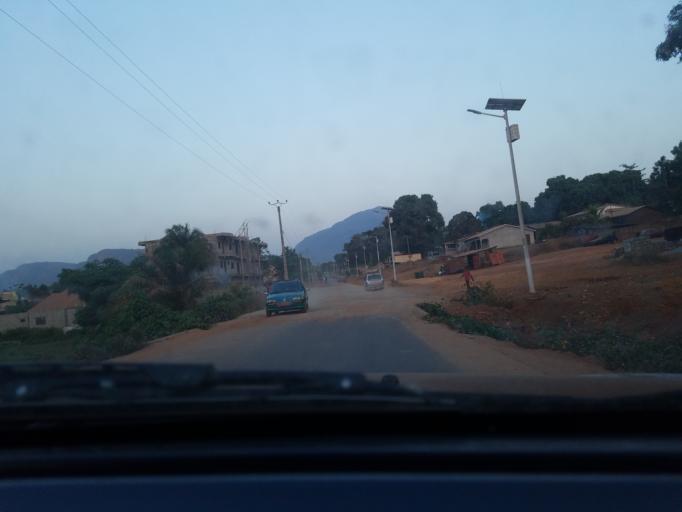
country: GN
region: Kindia
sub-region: Prefecture de Dubreka
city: Dubreka
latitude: 9.7890
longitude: -13.5139
